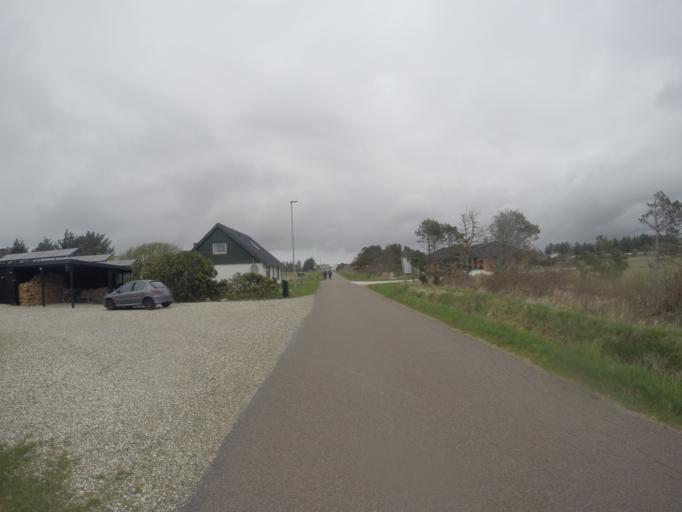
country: DK
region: North Denmark
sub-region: Thisted Kommune
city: Hurup
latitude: 56.9172
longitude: 8.3593
